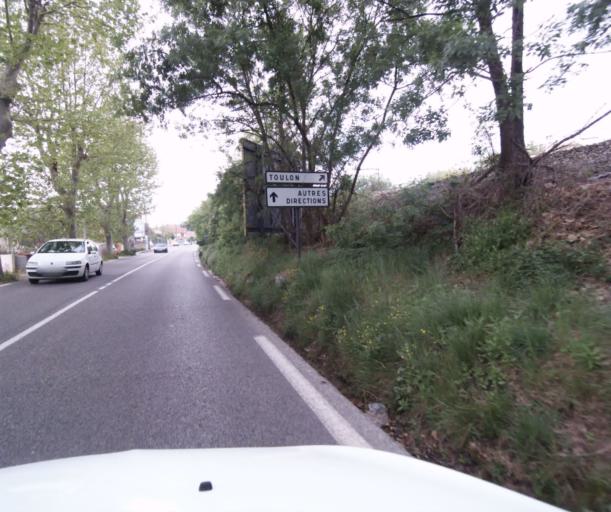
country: FR
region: Provence-Alpes-Cote d'Azur
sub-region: Departement du Var
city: La Valette-du-Var
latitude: 43.1153
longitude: 5.9850
